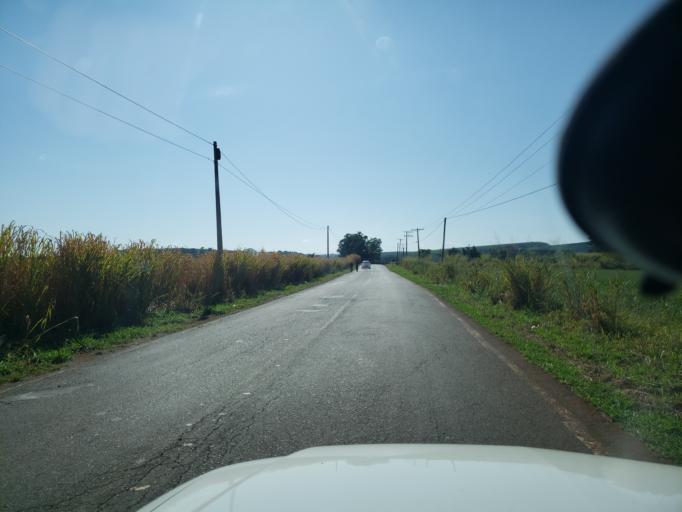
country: BR
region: Sao Paulo
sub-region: Moji-Guacu
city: Mogi-Gaucu
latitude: -22.3381
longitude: -46.8850
